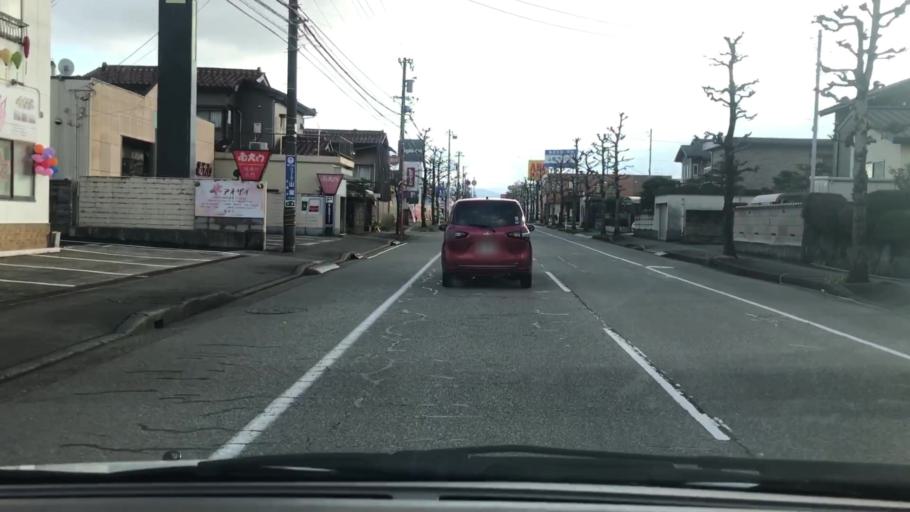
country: JP
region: Toyama
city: Toyama-shi
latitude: 36.6747
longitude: 137.2370
